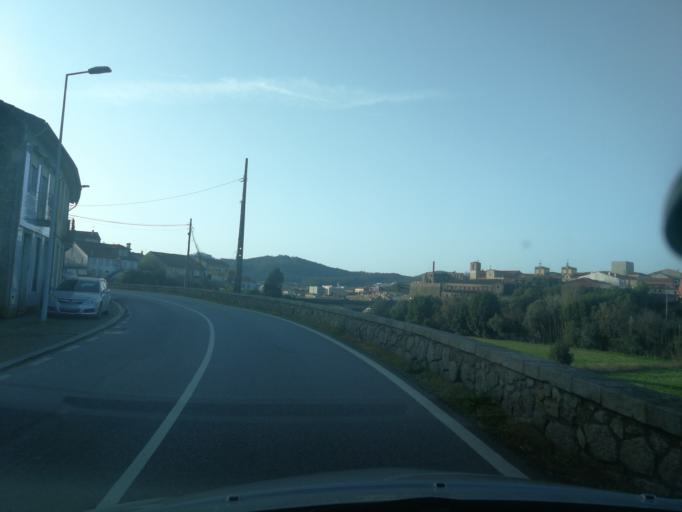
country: PT
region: Braga
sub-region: Barcelos
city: Barcelos
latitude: 41.5261
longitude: -8.6187
